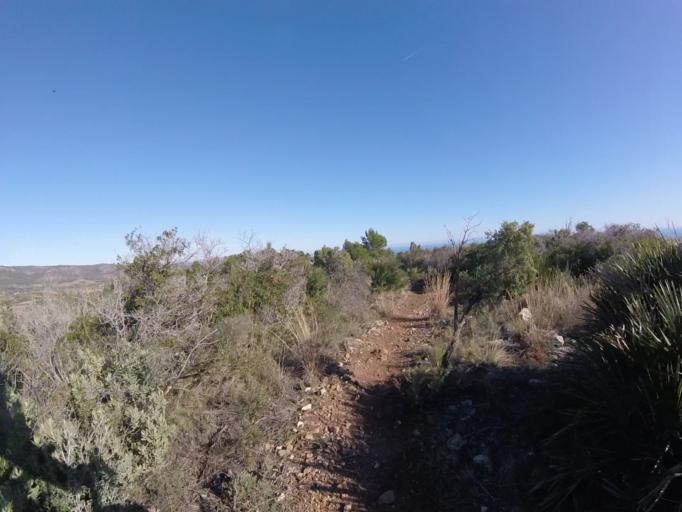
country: ES
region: Valencia
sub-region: Provincia de Castello
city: Orpesa/Oropesa del Mar
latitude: 40.1176
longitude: 0.1183
